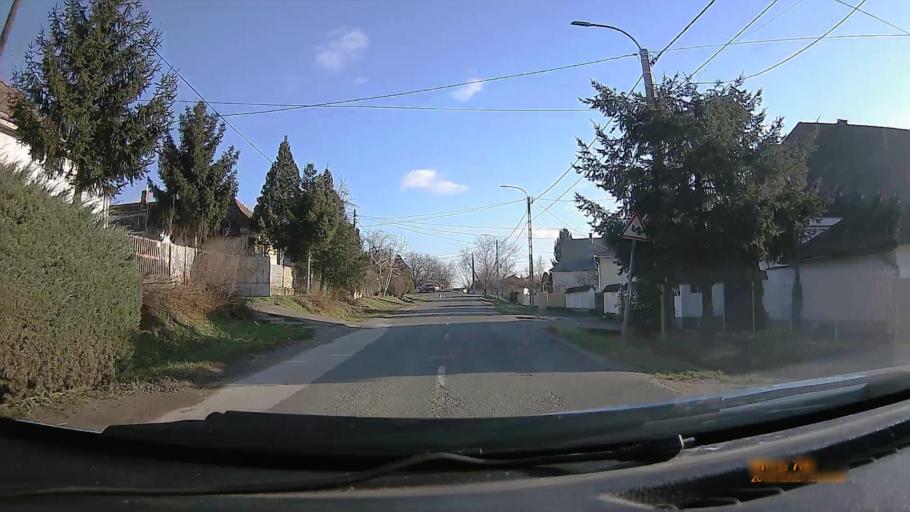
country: HU
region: Heves
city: Domoszlo
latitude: 47.8489
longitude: 20.1521
